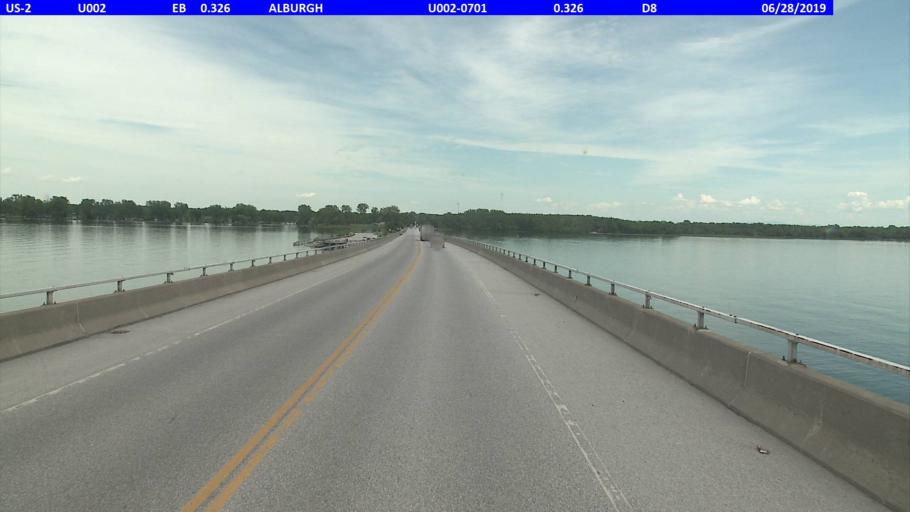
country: US
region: New York
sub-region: Clinton County
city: Rouses Point
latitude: 44.9982
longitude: -73.3429
